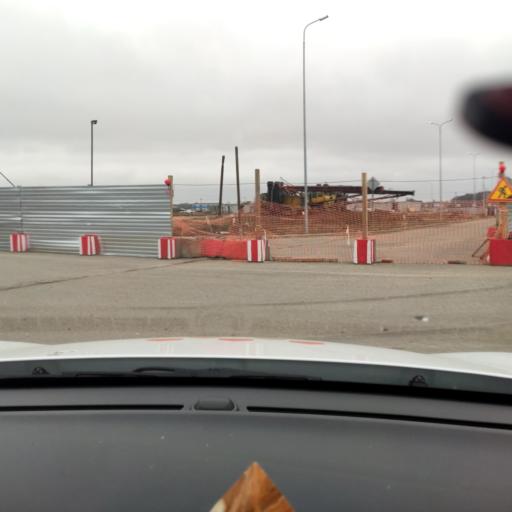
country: RU
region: Tatarstan
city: Osinovo
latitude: 55.8554
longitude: 48.9097
